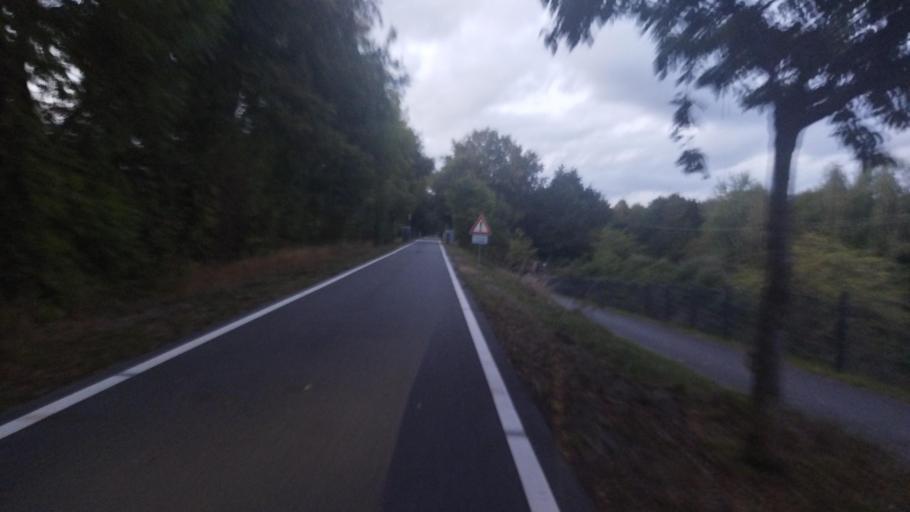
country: DE
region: North Rhine-Westphalia
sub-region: Regierungsbezirk Munster
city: Horstmar
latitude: 52.0970
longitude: 7.3299
